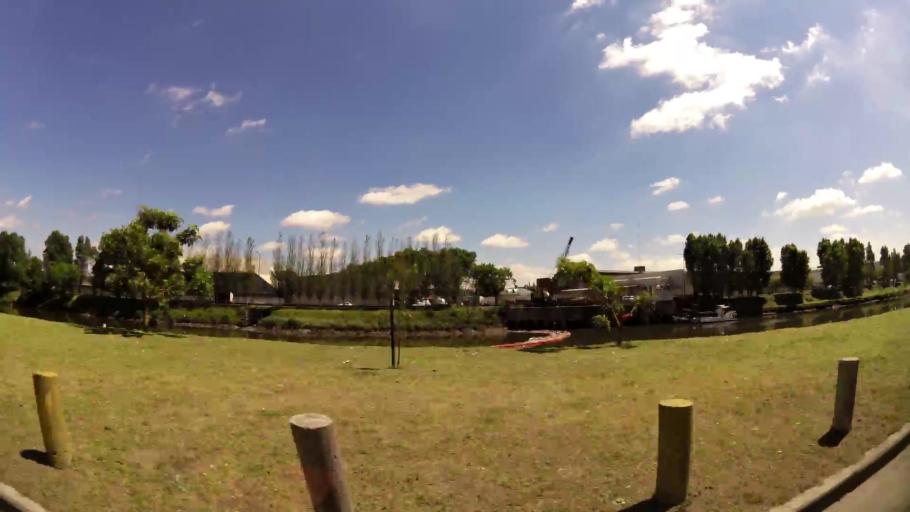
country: AR
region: Buenos Aires
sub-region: Partido de Lanus
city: Lanus
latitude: -34.6611
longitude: -58.4201
